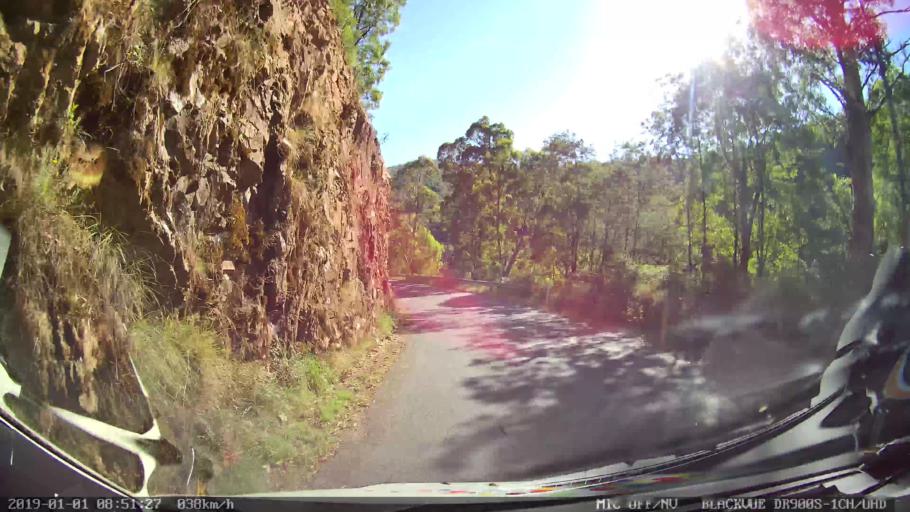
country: AU
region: New South Wales
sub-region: Snowy River
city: Jindabyne
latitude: -36.2713
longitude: 148.2011
